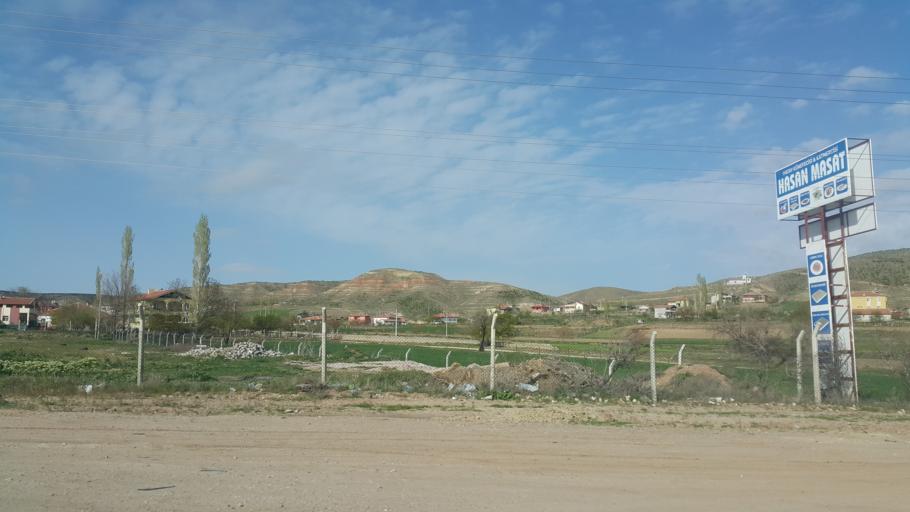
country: TR
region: Aksaray
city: Yesilova
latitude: 38.4481
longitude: 33.9324
